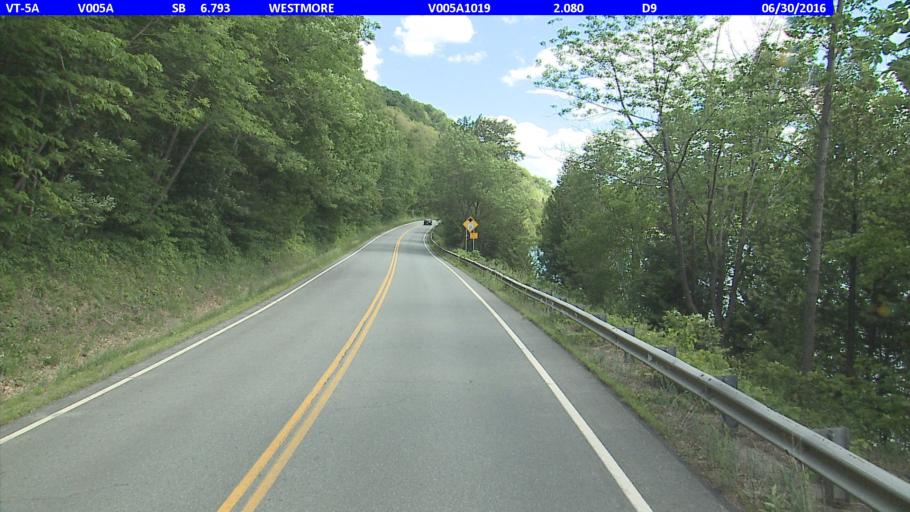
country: US
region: Vermont
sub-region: Caledonia County
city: Lyndonville
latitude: 44.7237
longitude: -72.0335
